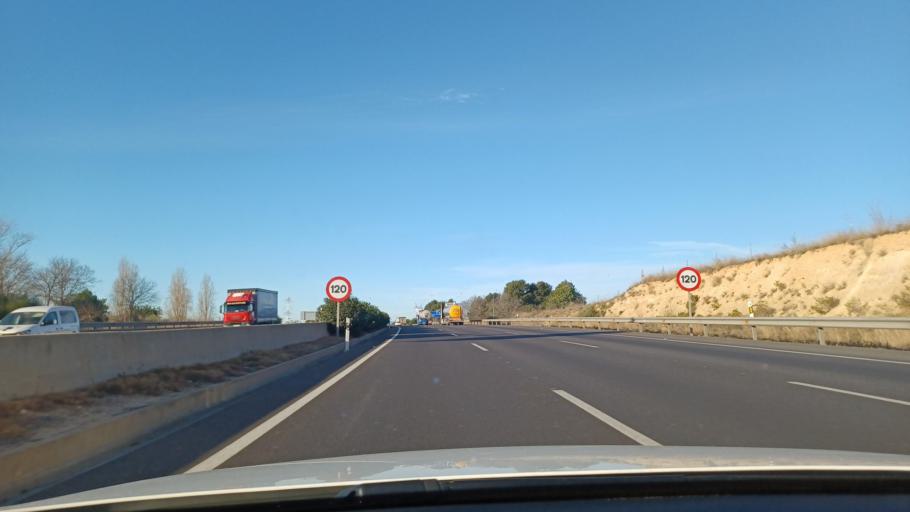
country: ES
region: Valencia
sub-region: Provincia de Valencia
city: Manises
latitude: 39.5046
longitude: -0.5187
